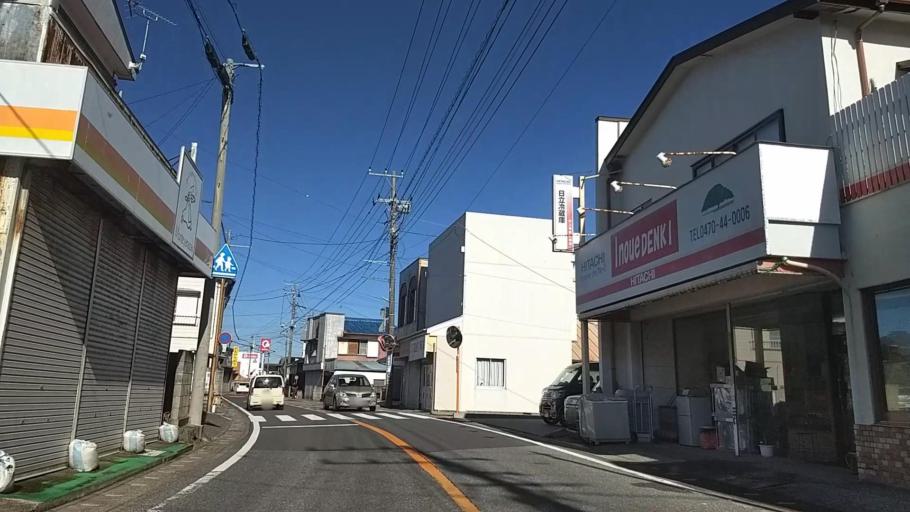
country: JP
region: Chiba
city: Tateyama
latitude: 34.9580
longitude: 139.9593
